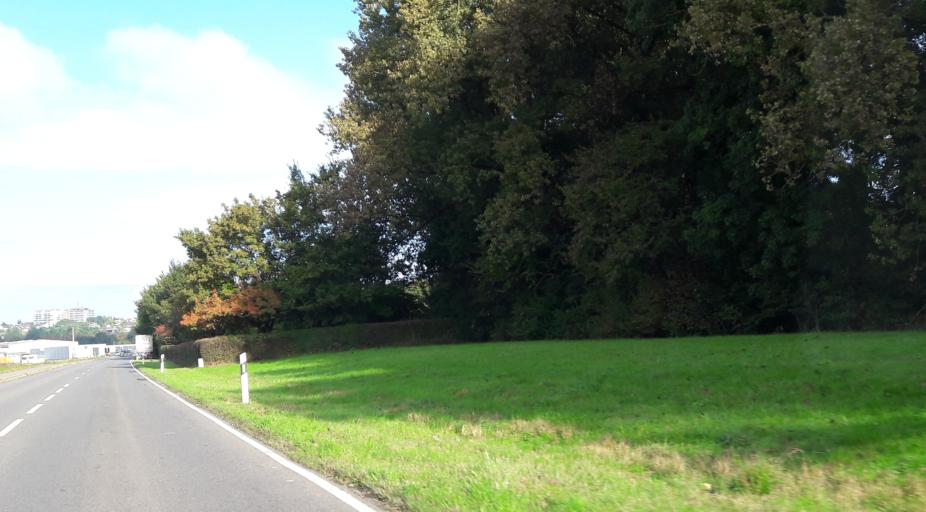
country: DE
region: Baden-Wuerttemberg
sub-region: Karlsruhe Region
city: Sinsheim
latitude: 49.2435
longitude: 8.9055
